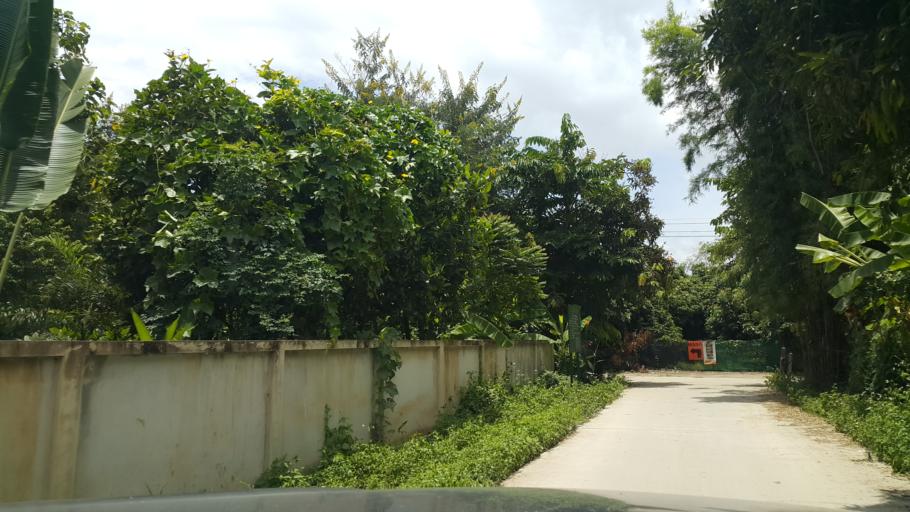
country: TH
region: Chiang Mai
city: Saraphi
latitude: 18.7339
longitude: 98.9945
